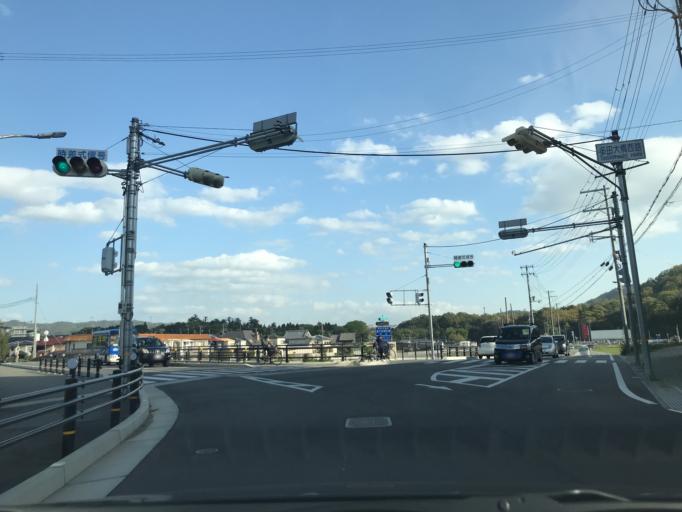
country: JP
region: Hyogo
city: Kawanishi
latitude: 34.8648
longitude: 135.3988
